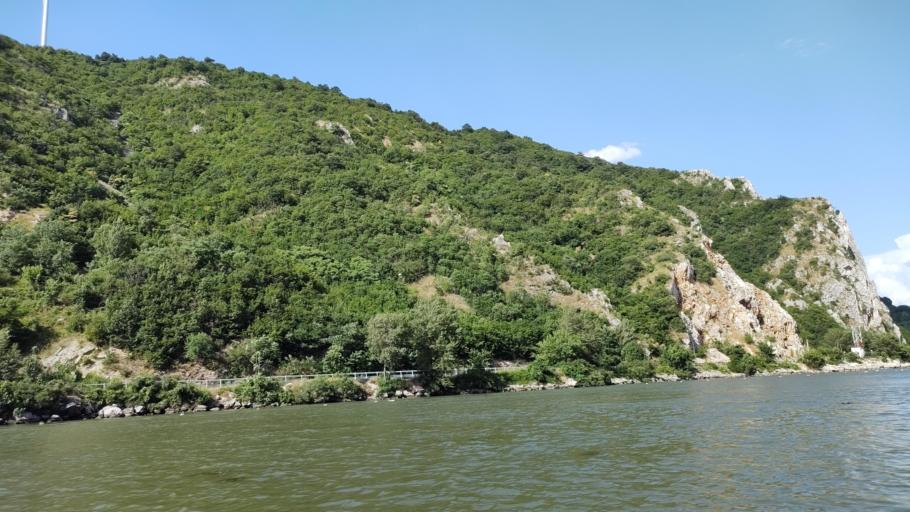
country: RO
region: Caras-Severin
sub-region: Comuna Pescari
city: Coronini
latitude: 44.6543
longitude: 21.7202
